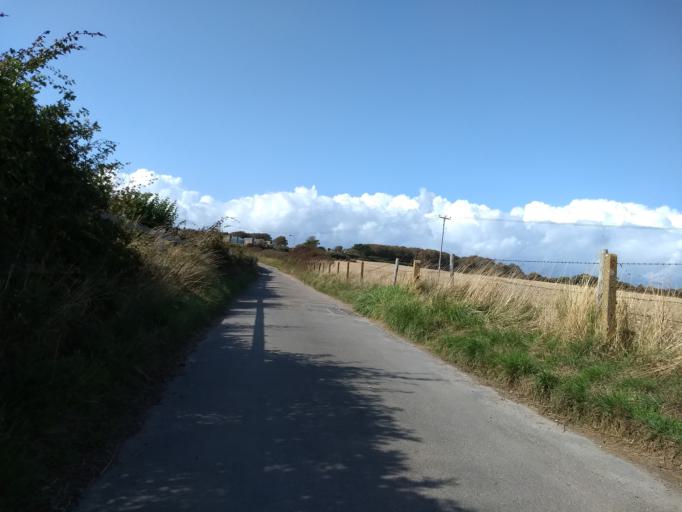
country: GB
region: England
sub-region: Isle of Wight
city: Totland
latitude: 50.6976
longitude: -1.5296
